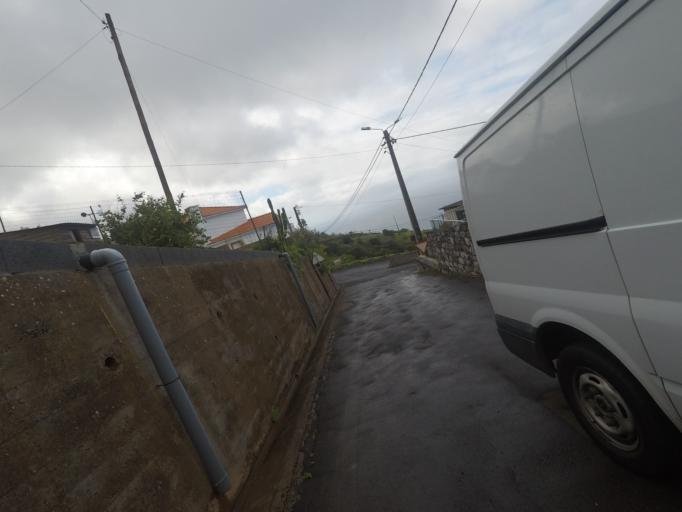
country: PT
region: Madeira
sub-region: Calheta
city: Faja da Ovelha
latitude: 32.7726
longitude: -17.2360
